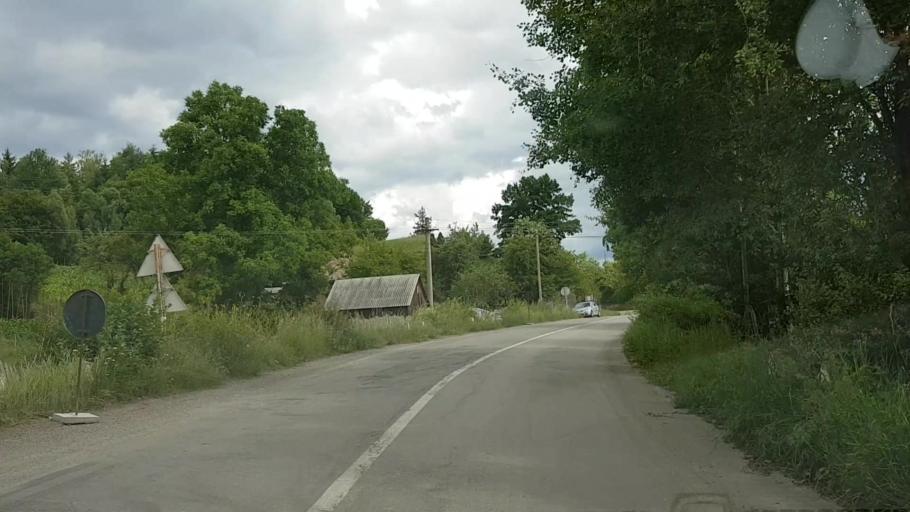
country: RO
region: Neamt
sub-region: Comuna Hangu
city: Hangu
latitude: 47.0469
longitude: 26.0492
